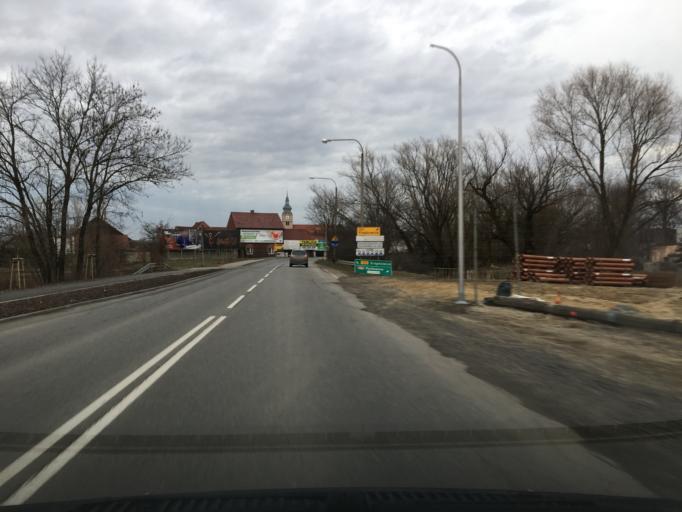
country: PL
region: Opole Voivodeship
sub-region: Powiat kedzierzynsko-kozielski
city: Kozle
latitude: 50.3435
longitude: 18.1658
